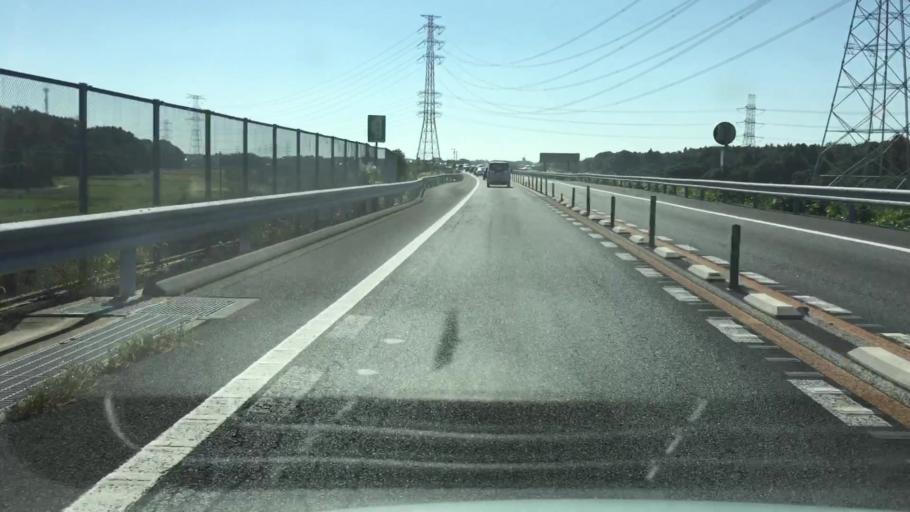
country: JP
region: Ibaraki
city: Ushiku
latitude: 36.0062
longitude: 140.1449
